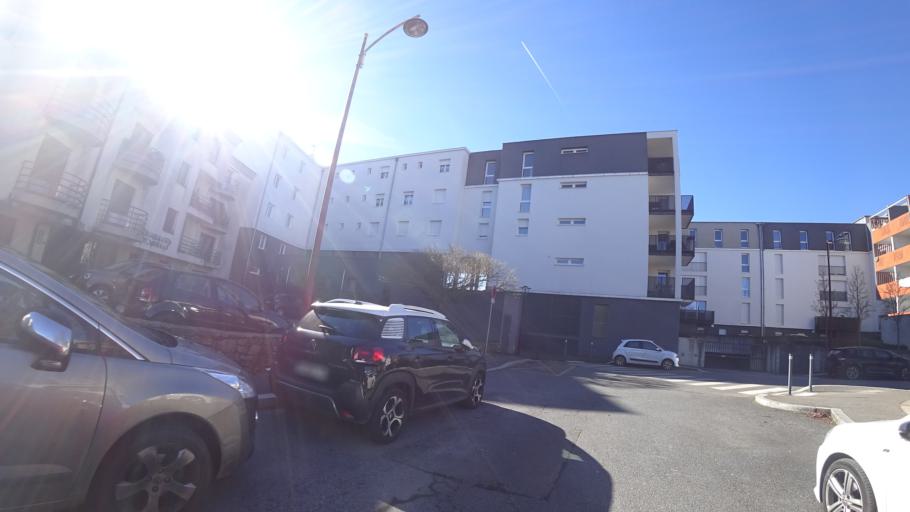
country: FR
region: Midi-Pyrenees
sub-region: Departement de l'Aveyron
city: Olemps
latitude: 44.3575
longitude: 2.5600
